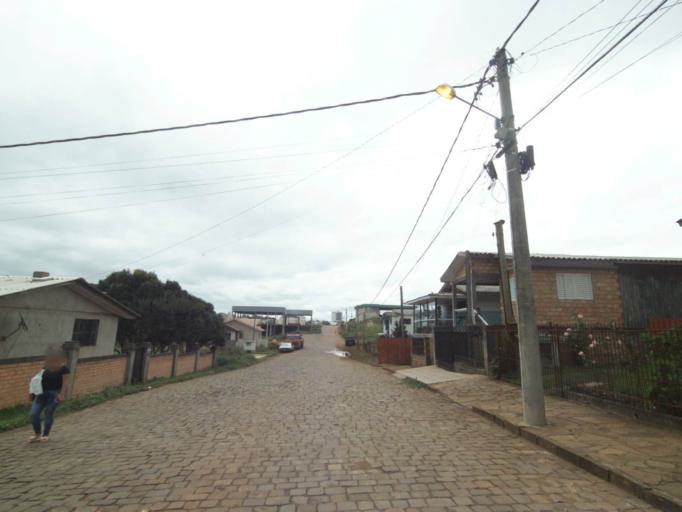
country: BR
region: Rio Grande do Sul
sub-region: Lagoa Vermelha
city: Lagoa Vermelha
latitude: -28.2139
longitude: -51.5074
